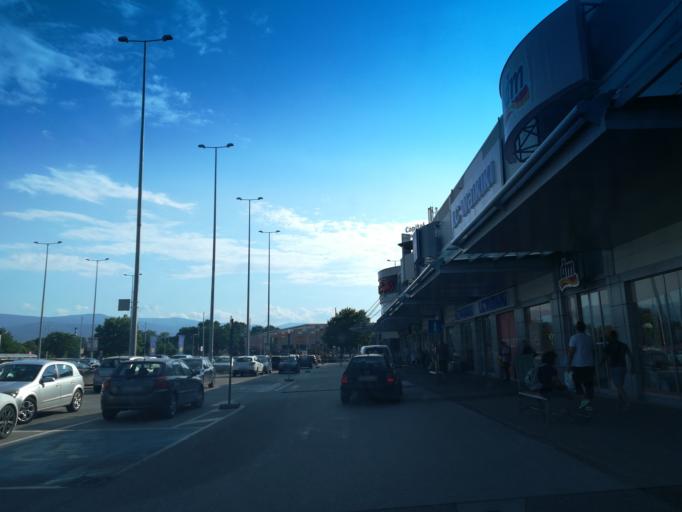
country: BG
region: Plovdiv
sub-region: Obshtina Plovdiv
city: Plovdiv
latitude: 42.1301
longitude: 24.7698
